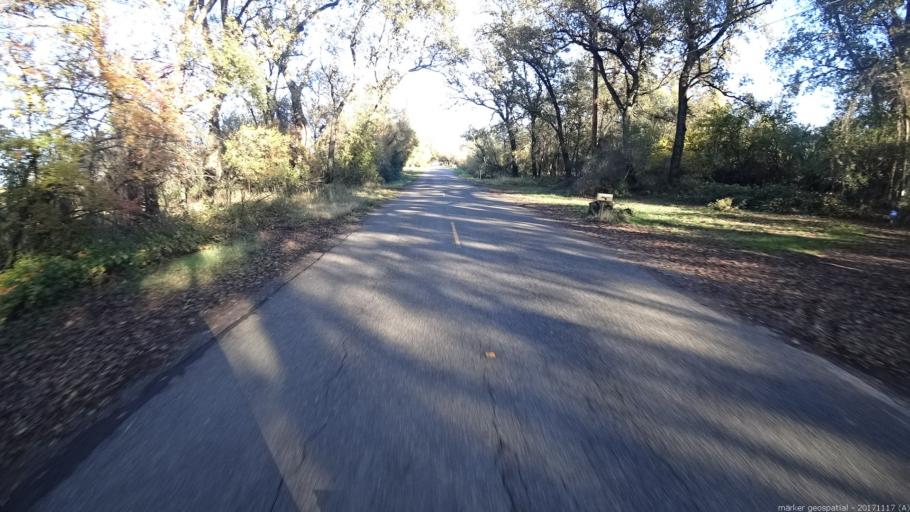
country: US
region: California
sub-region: Shasta County
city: Cottonwood
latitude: 40.3959
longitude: -122.2289
